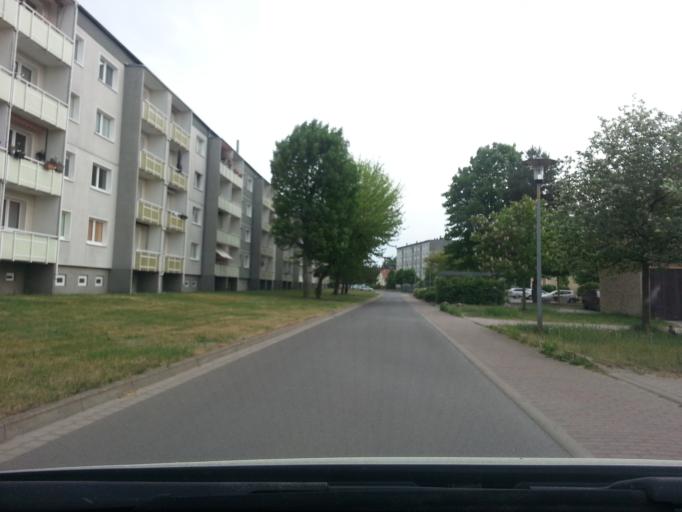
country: DE
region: Mecklenburg-Vorpommern
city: Torgelow
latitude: 53.6388
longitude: 14.0208
